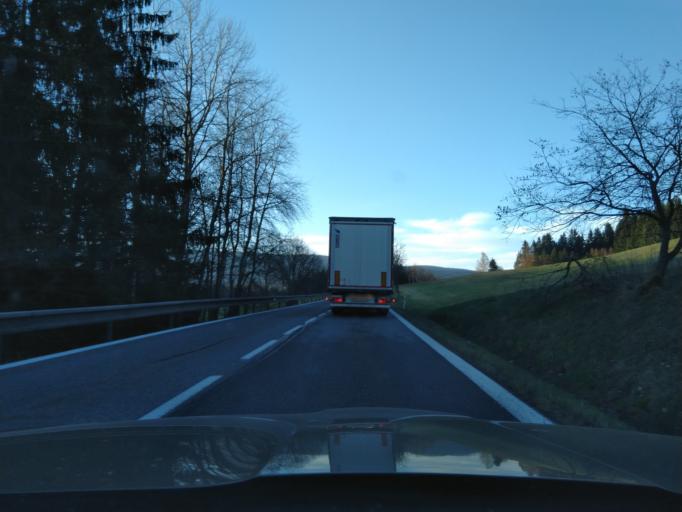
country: CZ
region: Jihocesky
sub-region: Okres Prachatice
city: Vimperk
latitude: 49.0227
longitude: 13.7674
